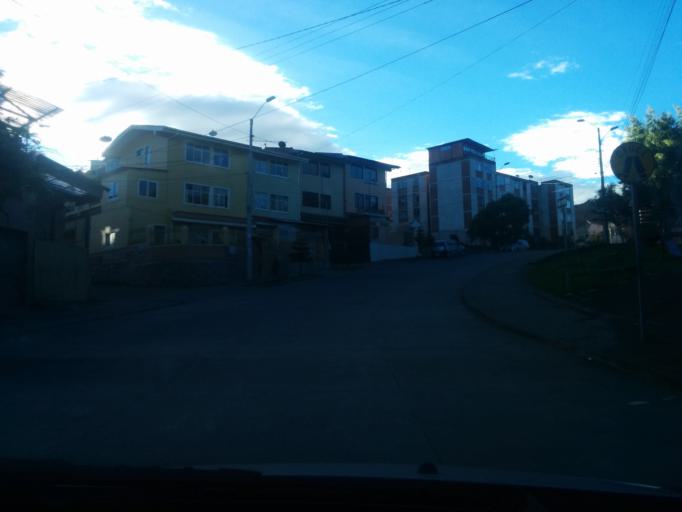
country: EC
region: Azuay
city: Cuenca
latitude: -2.8912
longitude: -78.9661
